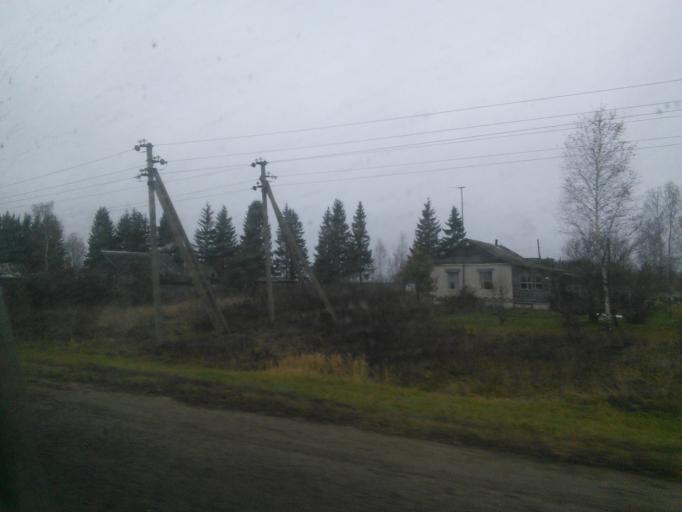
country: RU
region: Jaroslavl
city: Danilov
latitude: 57.9722
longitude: 40.0233
